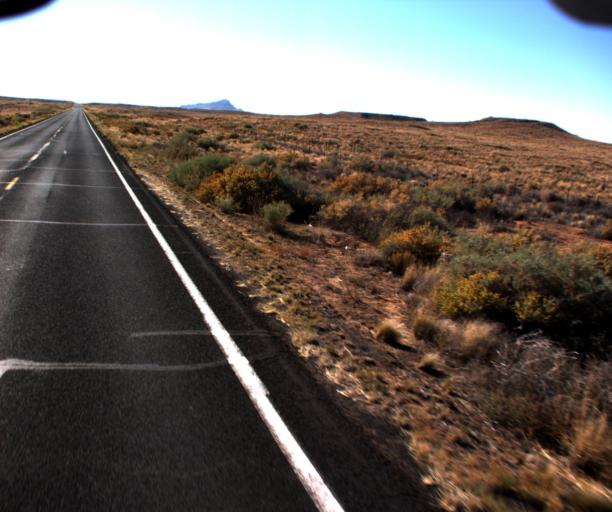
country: US
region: Arizona
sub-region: Navajo County
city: Dilkon
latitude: 35.5656
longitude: -110.4583
